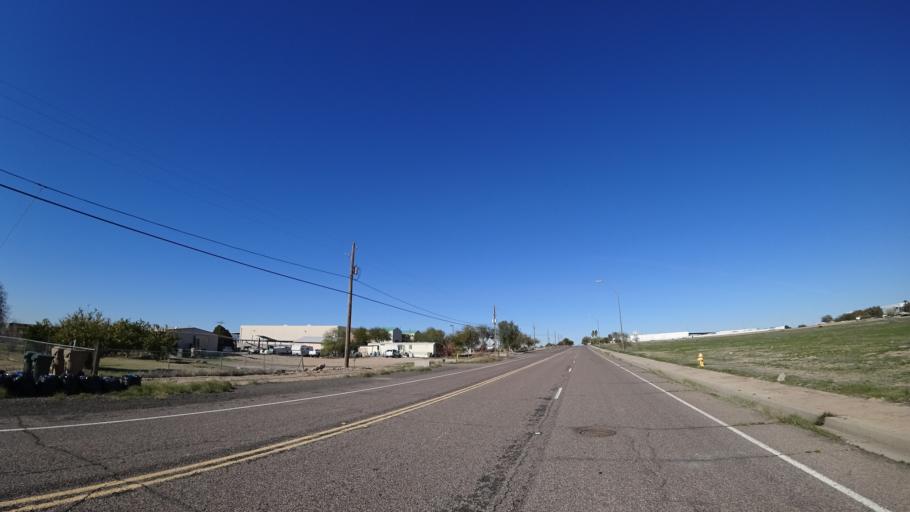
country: US
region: Arizona
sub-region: Maricopa County
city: Goodyear
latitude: 33.4075
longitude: -112.3751
